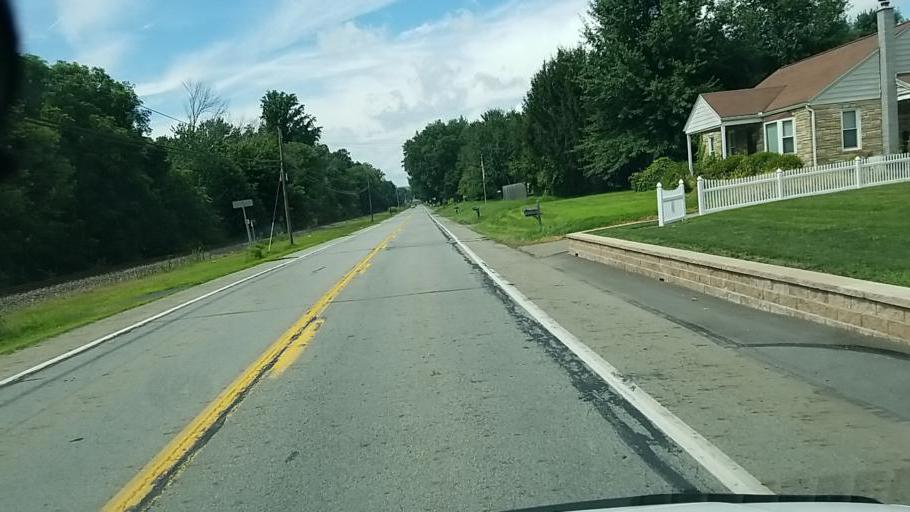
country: US
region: Pennsylvania
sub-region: Dauphin County
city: Millersburg
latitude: 40.4963
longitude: -76.9411
